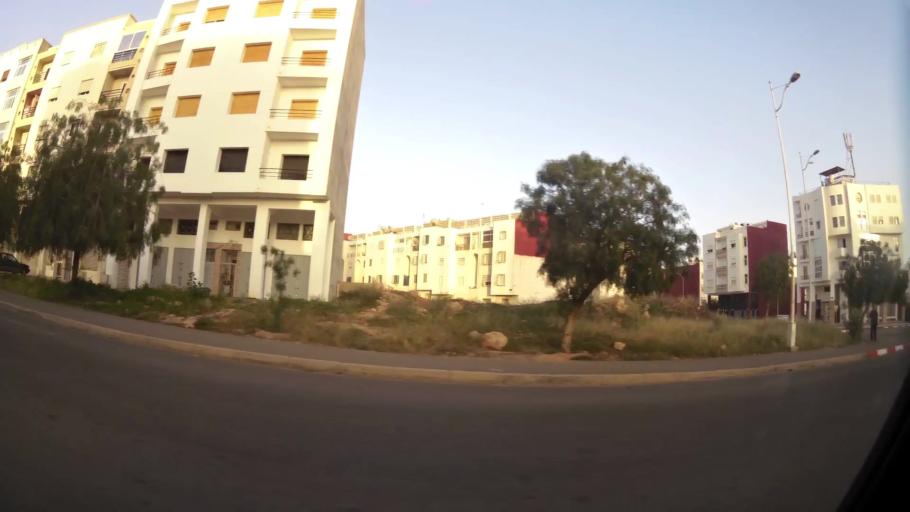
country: MA
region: Oued ed Dahab-Lagouira
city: Dakhla
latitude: 30.3932
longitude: -9.5655
